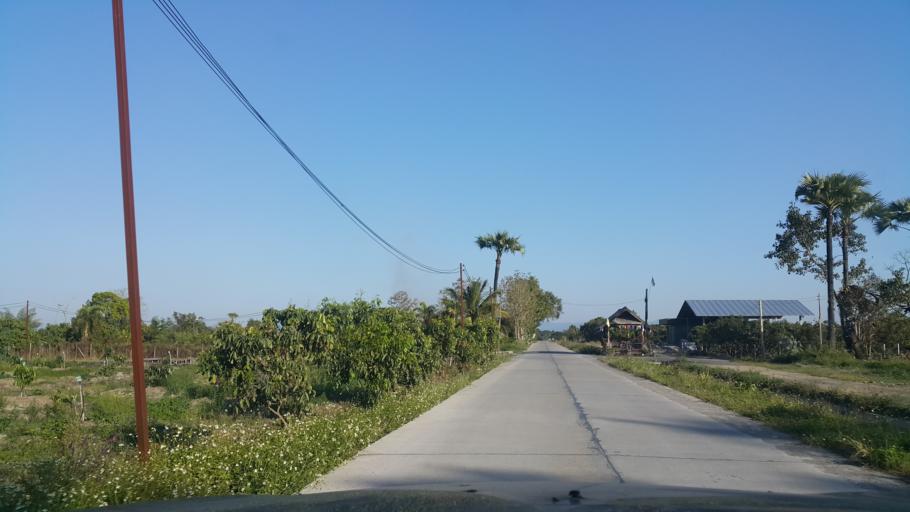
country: TH
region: Chiang Mai
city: Hang Dong
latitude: 18.6773
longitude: 98.9596
